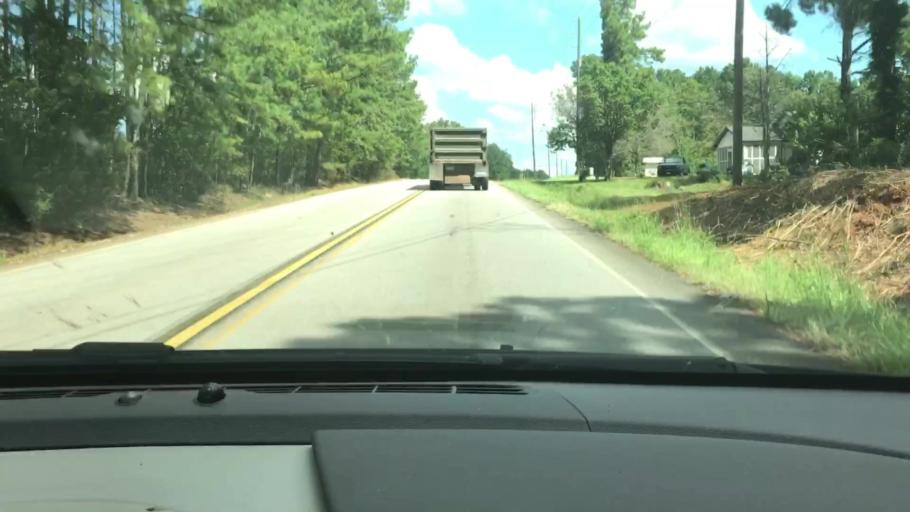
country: US
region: Alabama
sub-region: Chambers County
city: Valley
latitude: 32.8437
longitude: -85.0351
